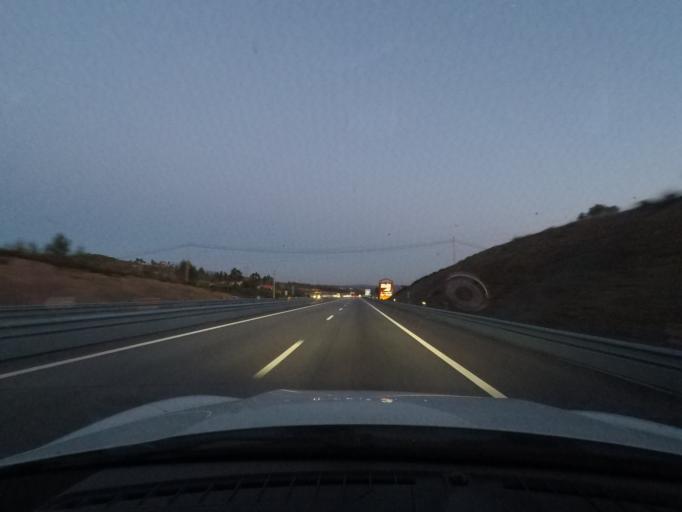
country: PT
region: Porto
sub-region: Paredes
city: Recarei
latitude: 41.1593
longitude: -8.4433
